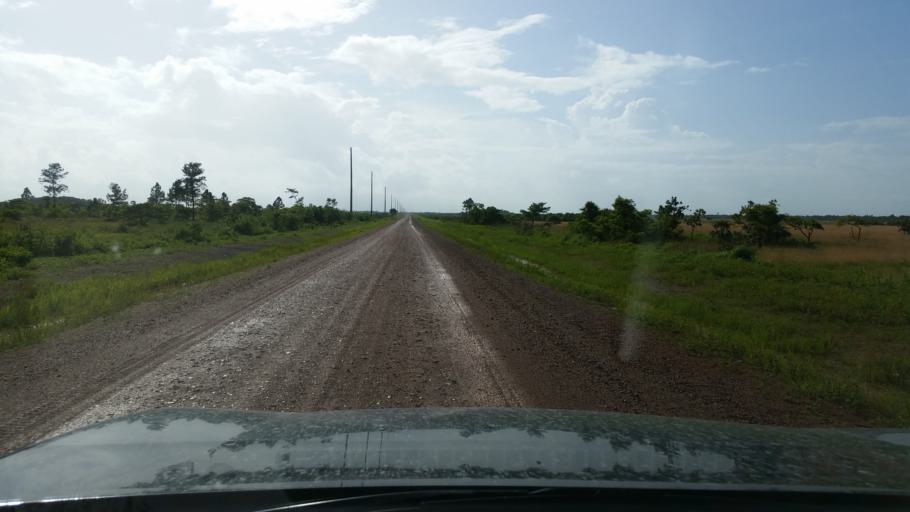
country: NI
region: Atlantico Norte (RAAN)
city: Puerto Cabezas
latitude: 14.1101
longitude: -83.6062
